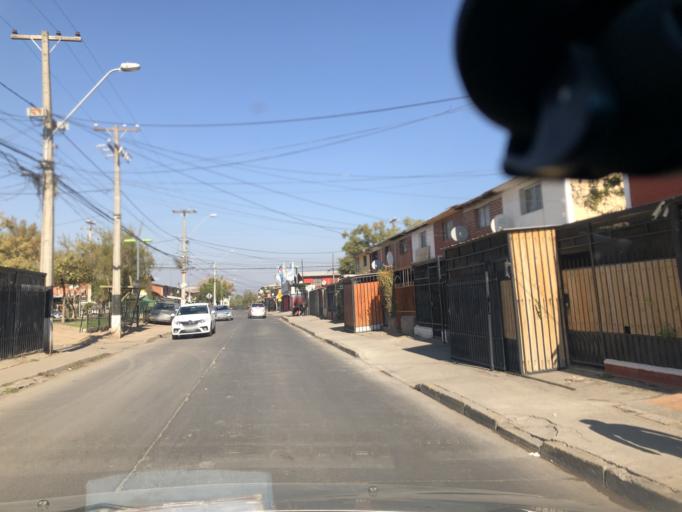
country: CL
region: Santiago Metropolitan
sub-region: Provincia de Cordillera
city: Puente Alto
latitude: -33.6239
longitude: -70.5961
